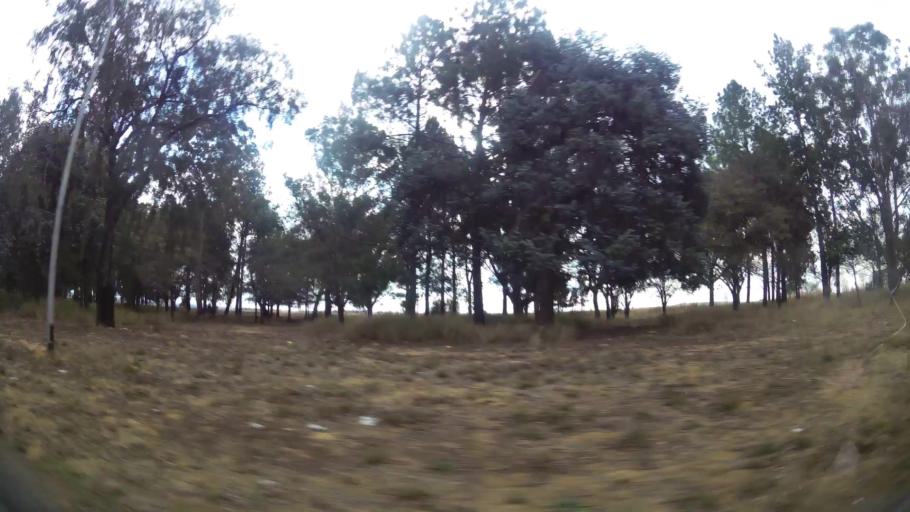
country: ZA
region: Orange Free State
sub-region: Fezile Dabi District Municipality
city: Sasolburg
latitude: -26.7919
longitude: 27.8157
